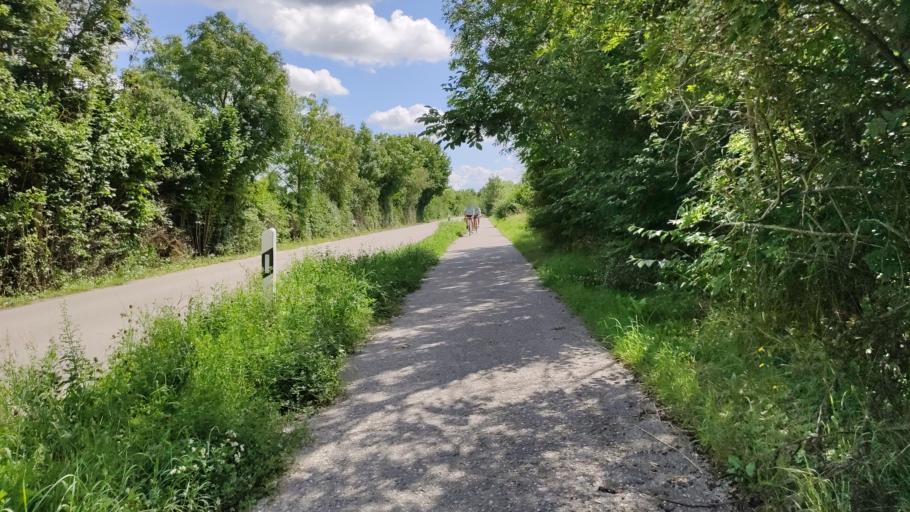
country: DE
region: Bavaria
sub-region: Swabia
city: Konigsbrunn
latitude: 48.2473
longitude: 10.8931
